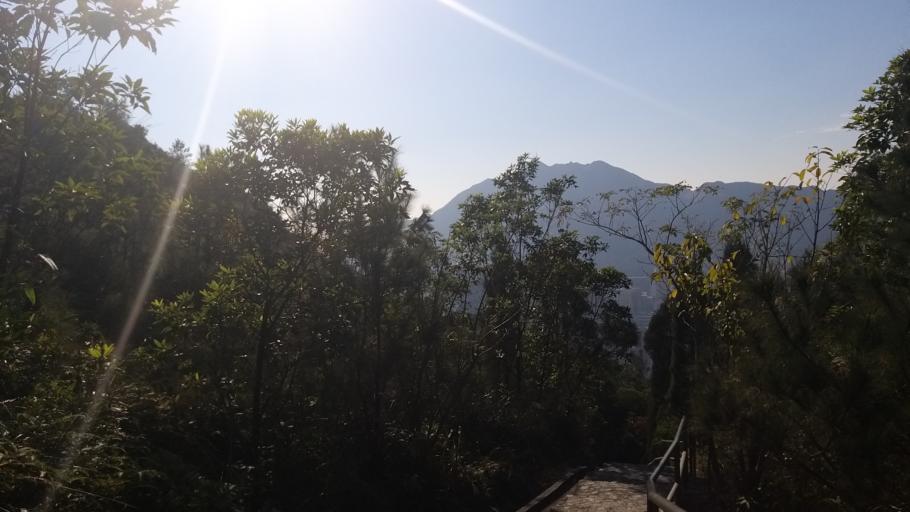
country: HK
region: Tuen Mun
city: Tuen Mun
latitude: 22.4001
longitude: 113.9863
